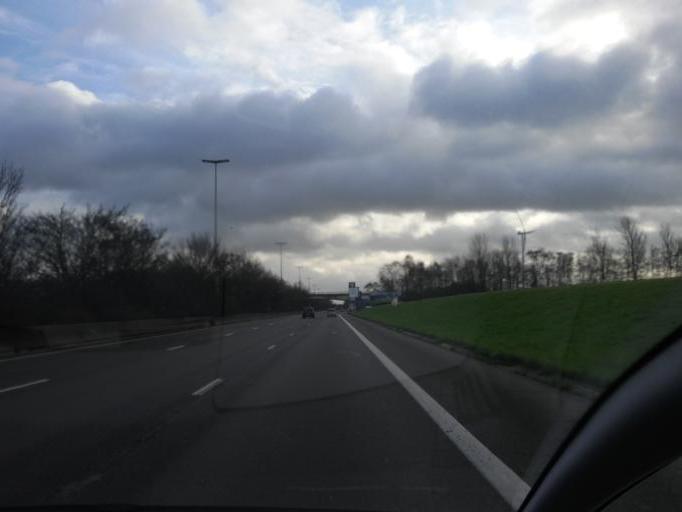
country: BE
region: Wallonia
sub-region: Province du Brabant Wallon
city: Perwez
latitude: 50.6040
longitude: 4.7856
